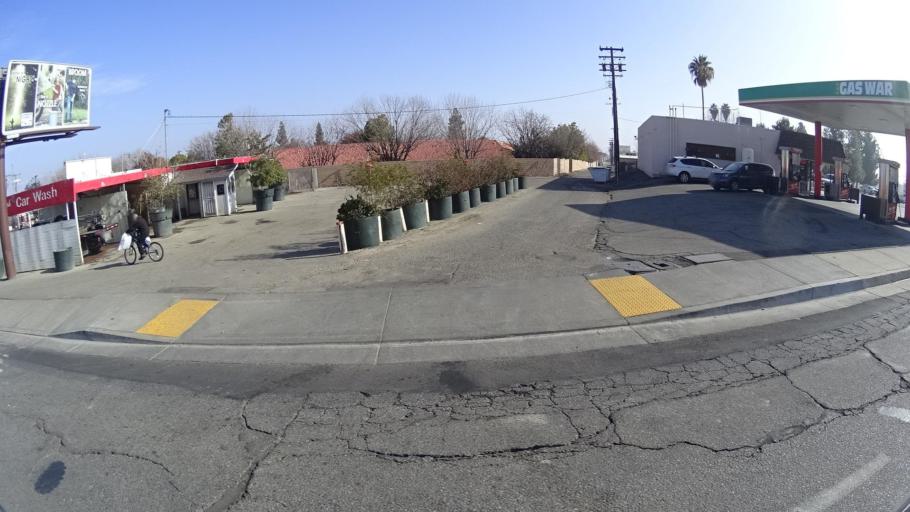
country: US
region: California
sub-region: Kern County
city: Taft
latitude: 35.1433
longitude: -119.4651
